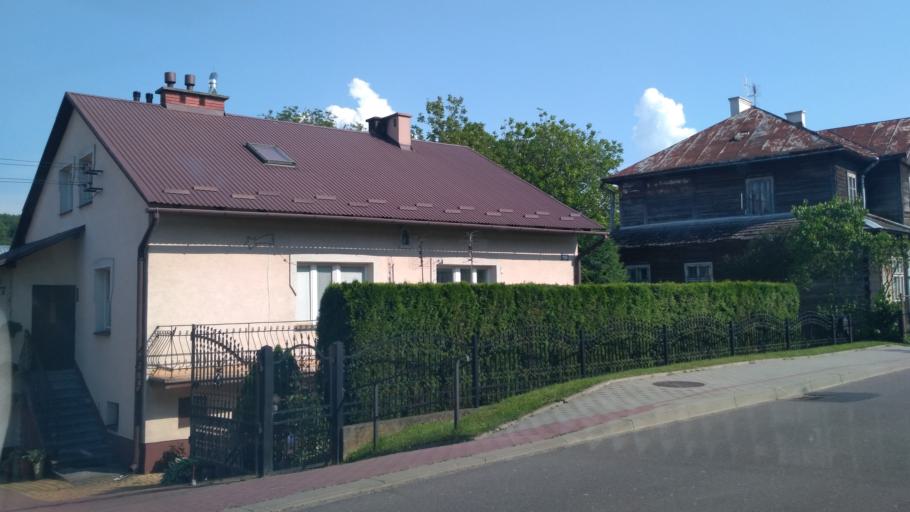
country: PL
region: Subcarpathian Voivodeship
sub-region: Powiat jaroslawski
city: Pruchnik
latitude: 49.8968
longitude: 22.5018
